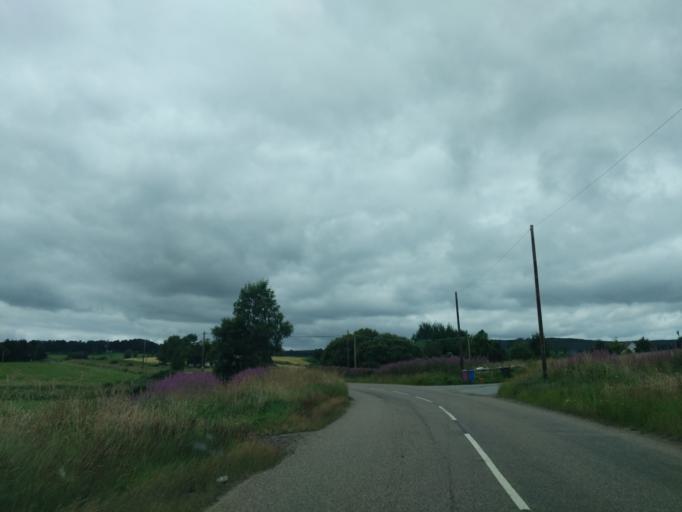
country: GB
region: Scotland
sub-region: Moray
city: Rothes
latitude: 57.4905
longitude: -3.2336
